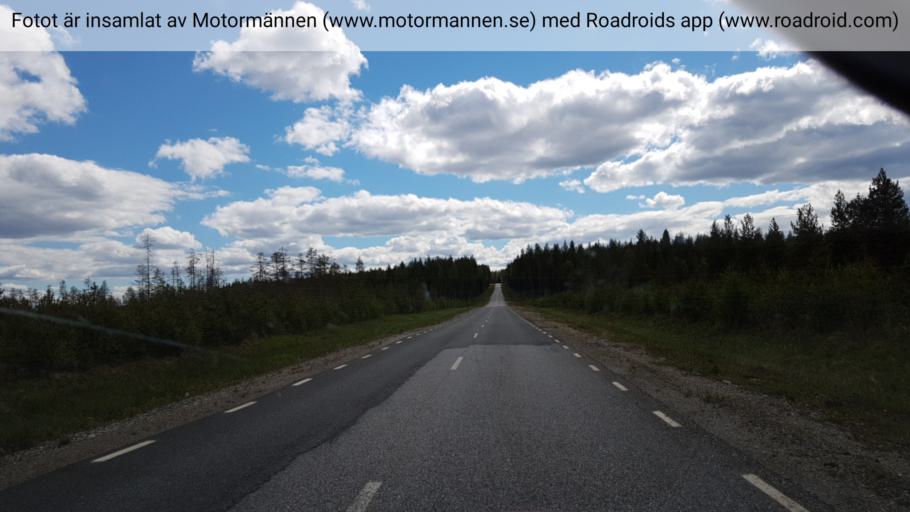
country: SE
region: Vaesterbotten
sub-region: Skelleftea Kommun
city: Langsele
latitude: 64.7076
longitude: 19.9879
